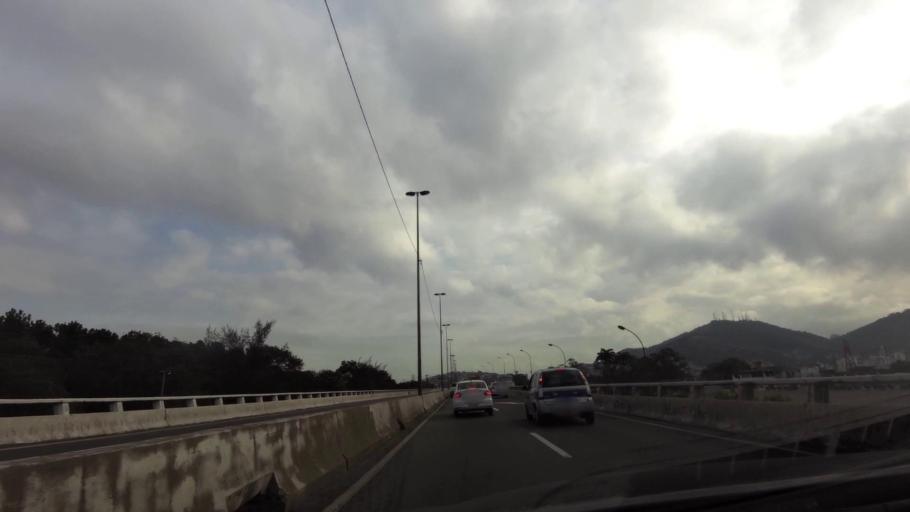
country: BR
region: Espirito Santo
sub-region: Vitoria
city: Vitoria
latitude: -20.3316
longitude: -40.3547
